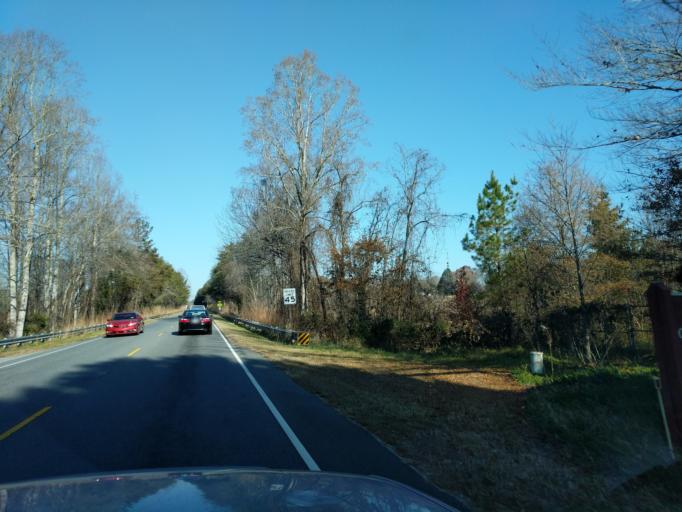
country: US
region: North Carolina
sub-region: Rutherford County
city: Rutherfordton
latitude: 35.3931
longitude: -81.9613
